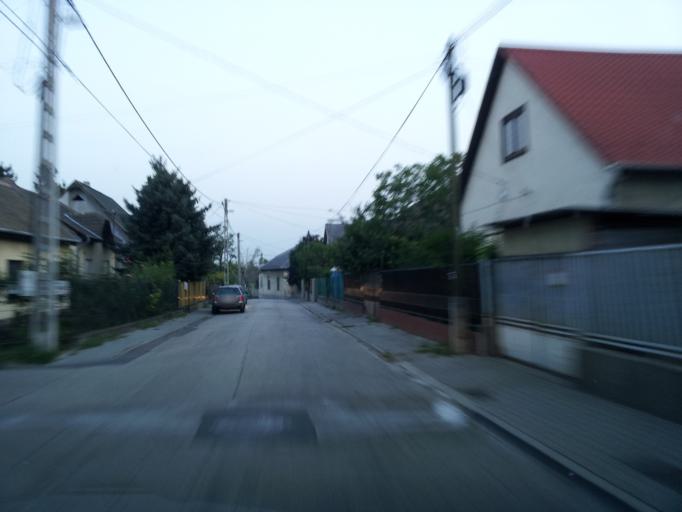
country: HU
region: Budapest
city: Budapest XXII. keruelet
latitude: 47.4191
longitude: 19.0277
